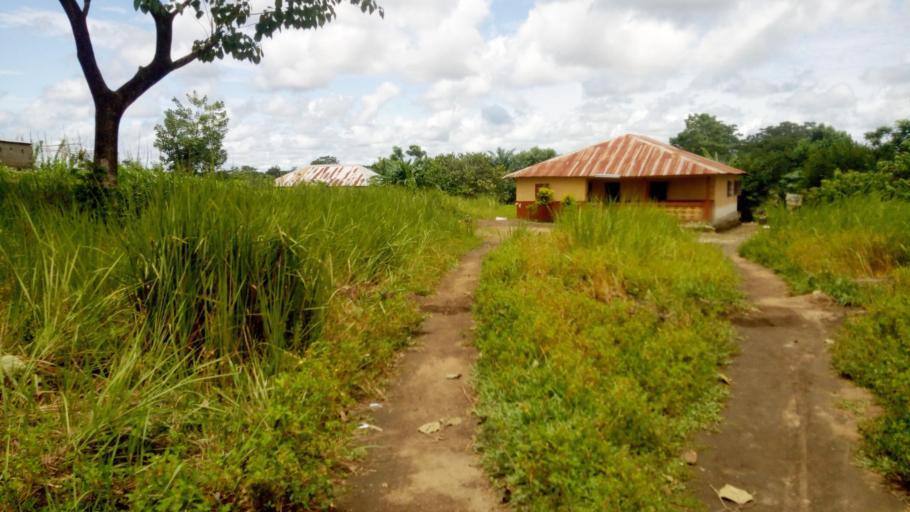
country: SL
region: Northern Province
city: Magburaka
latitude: 8.7127
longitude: -11.9561
